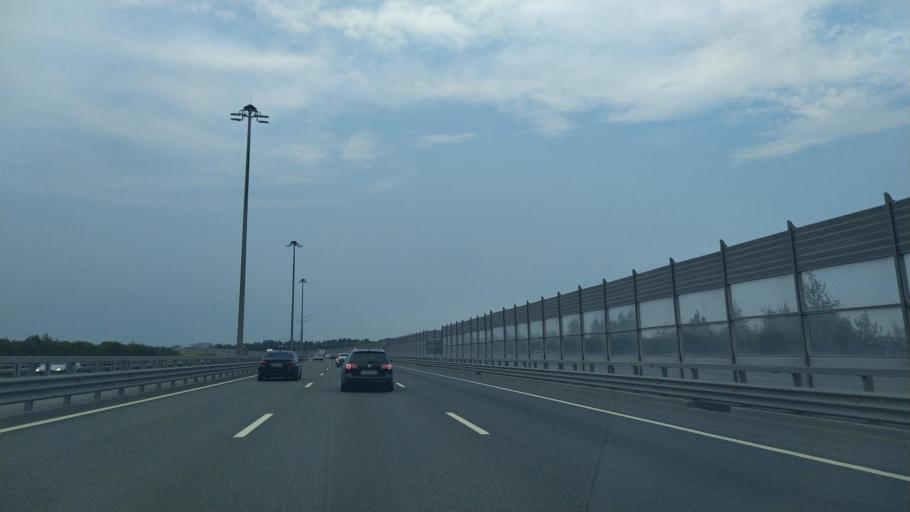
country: RU
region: St.-Petersburg
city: Levashovo
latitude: 60.0853
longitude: 30.2224
